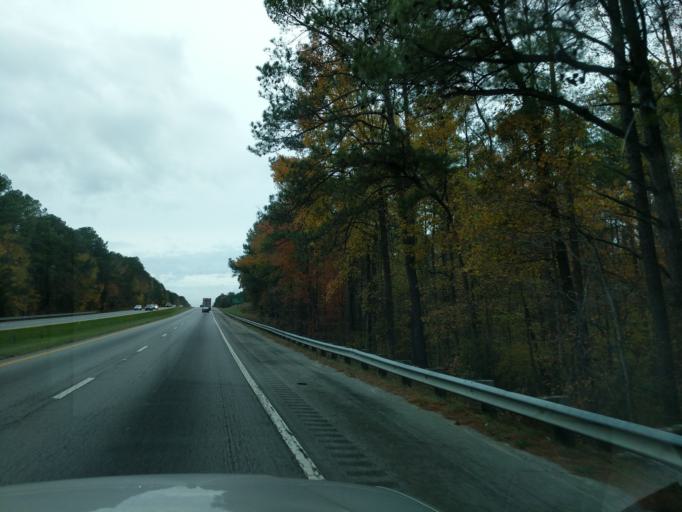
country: US
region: South Carolina
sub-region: Newberry County
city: Newberry
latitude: 34.3351
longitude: -81.6160
